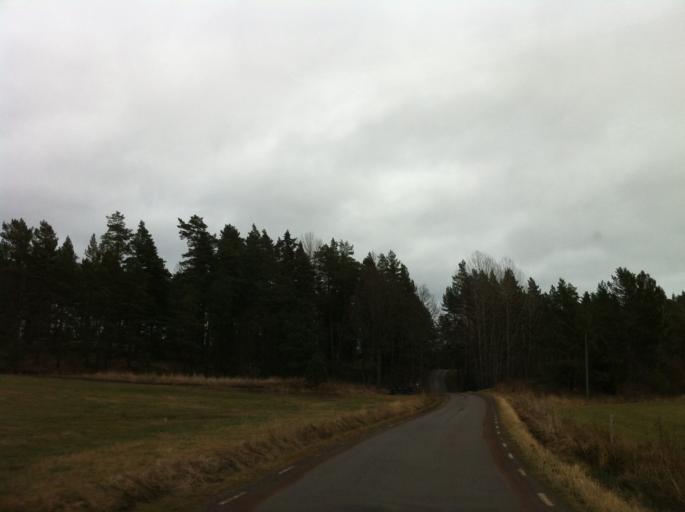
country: SE
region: Kalmar
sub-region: Vasterviks Kommun
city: Forserum
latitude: 57.9214
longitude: 16.5729
